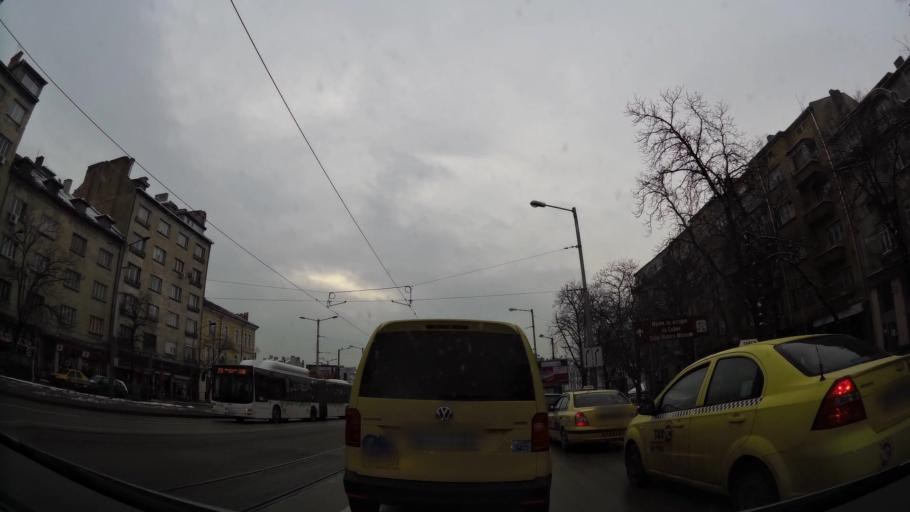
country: BG
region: Sofia-Capital
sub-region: Stolichna Obshtina
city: Sofia
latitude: 42.7062
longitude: 23.3235
